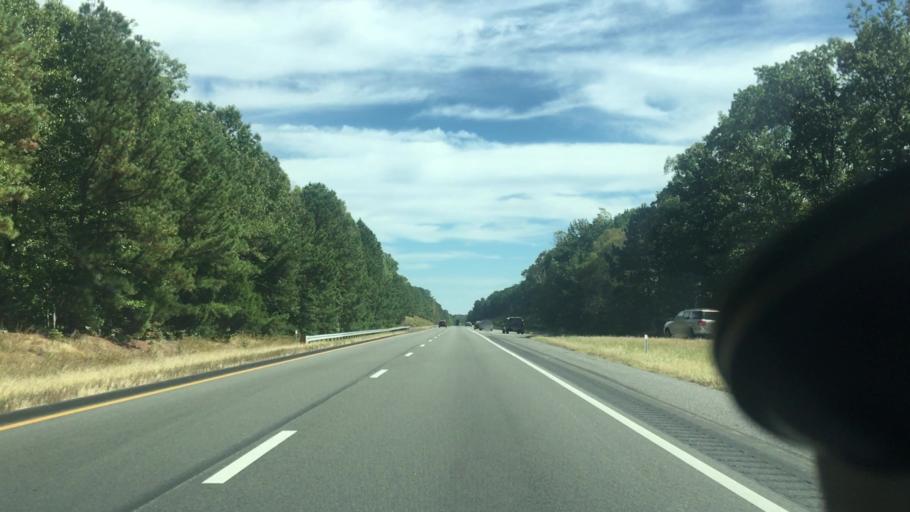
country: US
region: Virginia
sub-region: Chesterfield County
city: Chesterfield
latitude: 37.4084
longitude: -77.5621
